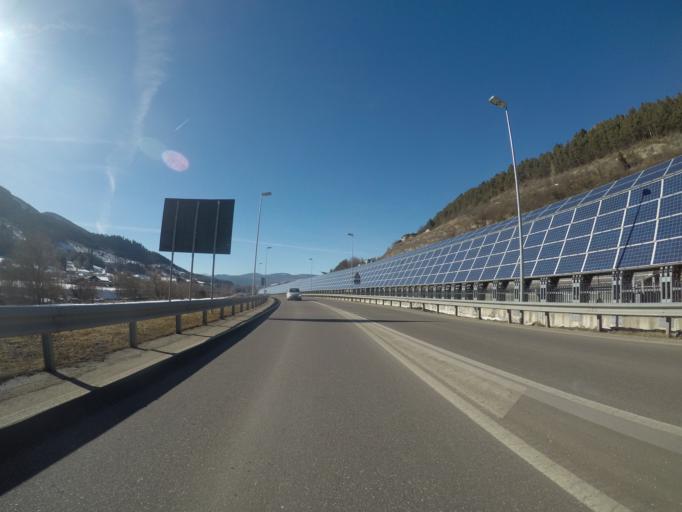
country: IT
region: Trentino-Alto Adige
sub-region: Provincia di Trento
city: Tesero
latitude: 46.2851
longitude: 11.5231
